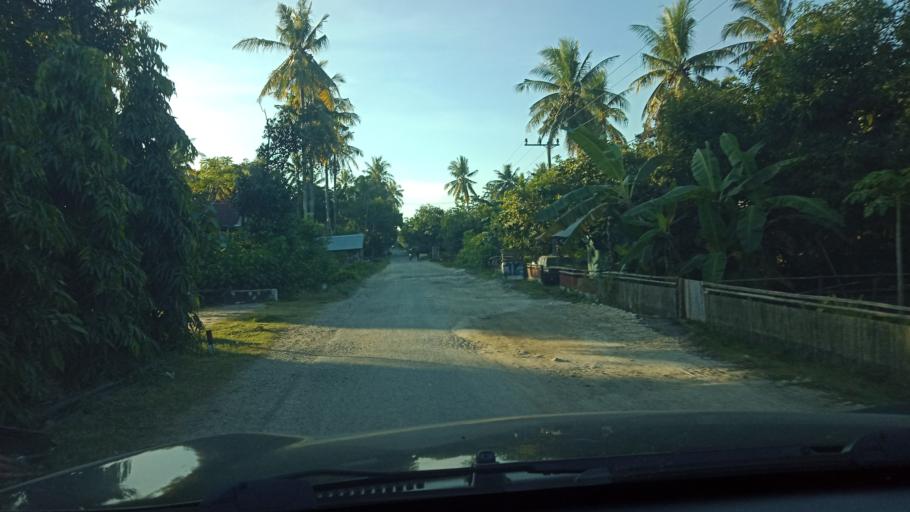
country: ID
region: South Sulawesi
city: Watampone
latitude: -4.4258
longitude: 120.3329
